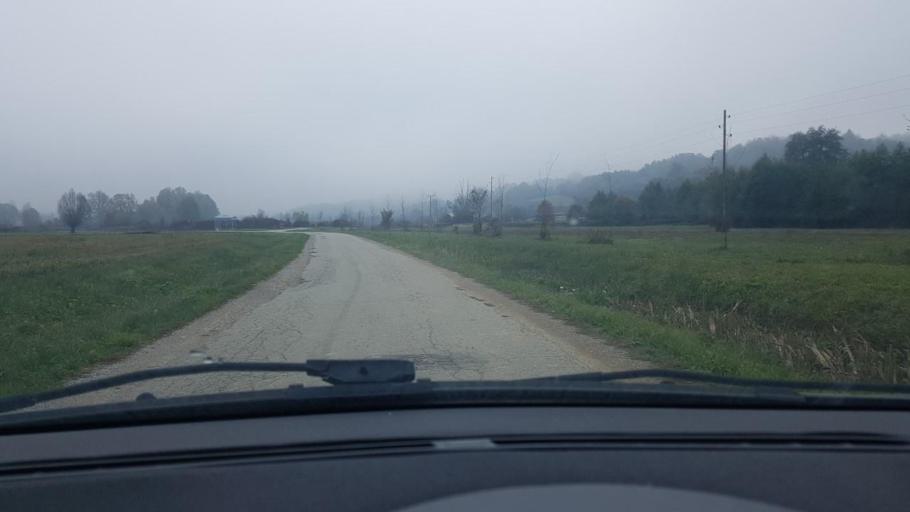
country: HR
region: Krapinsko-Zagorska
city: Zlatar
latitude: 46.1002
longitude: 16.1746
